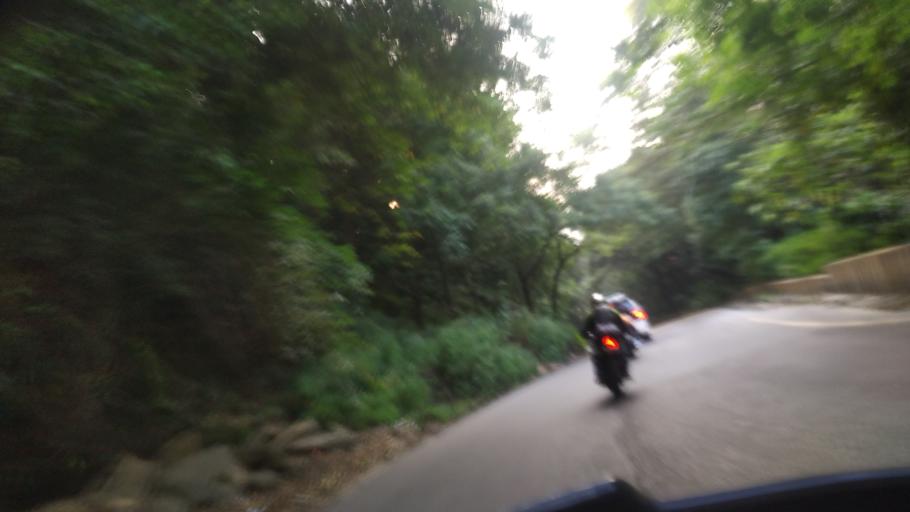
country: IN
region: Kerala
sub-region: Wayanad
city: Kalpetta
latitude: 11.5052
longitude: 76.0301
